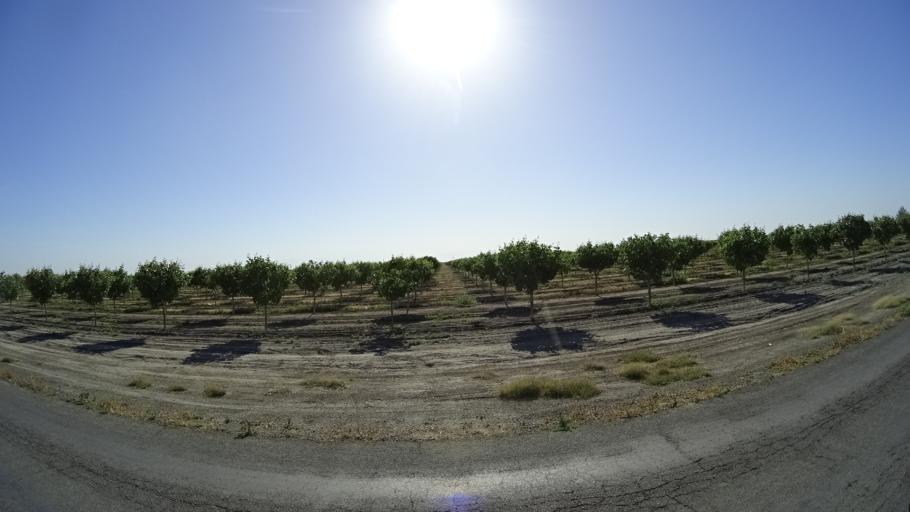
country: US
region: California
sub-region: Kings County
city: Corcoran
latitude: 36.1251
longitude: -119.5633
